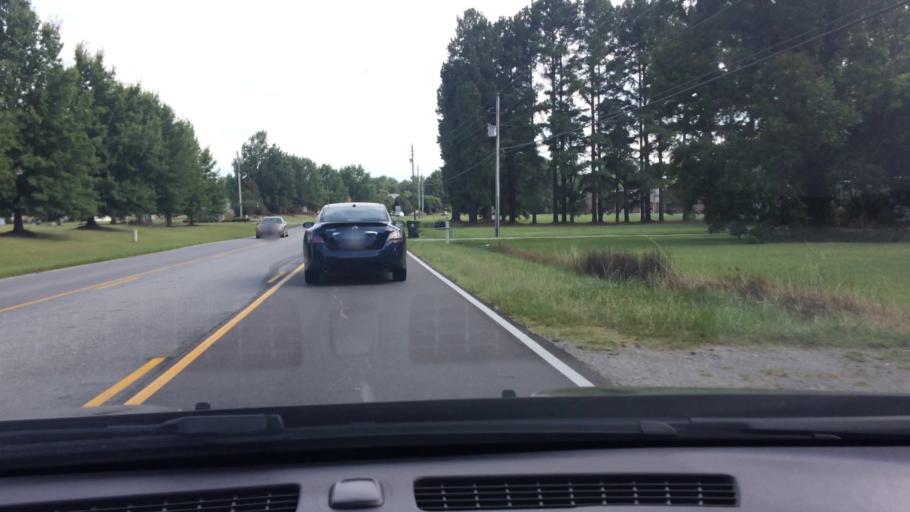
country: US
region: North Carolina
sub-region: Pitt County
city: Windsor
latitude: 35.5474
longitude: -77.3838
